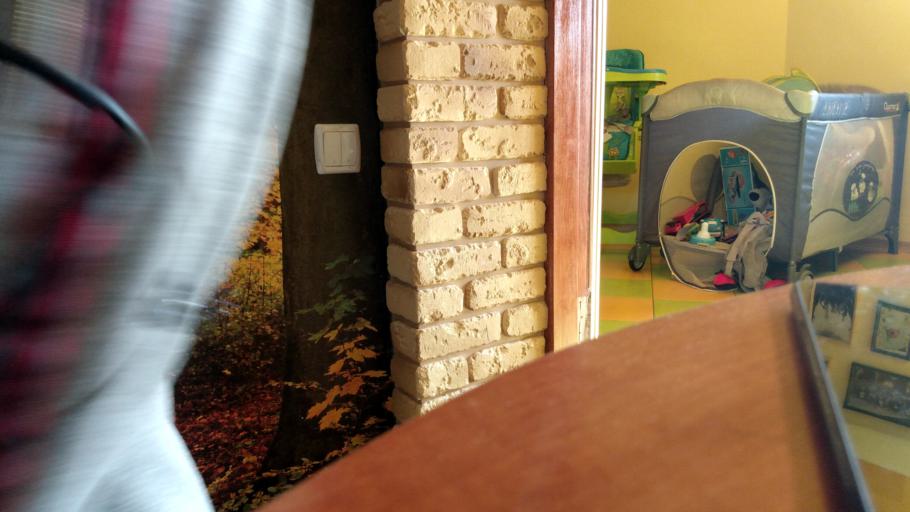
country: RU
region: Tverskaya
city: Gorodnya
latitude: 56.7836
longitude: 36.2697
